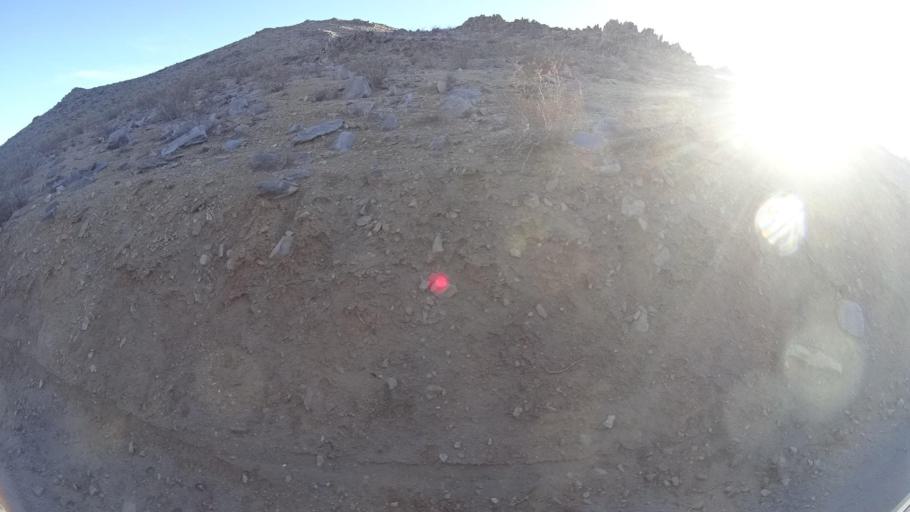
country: US
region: California
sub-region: Kern County
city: Ridgecrest
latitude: 35.5789
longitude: -117.6603
